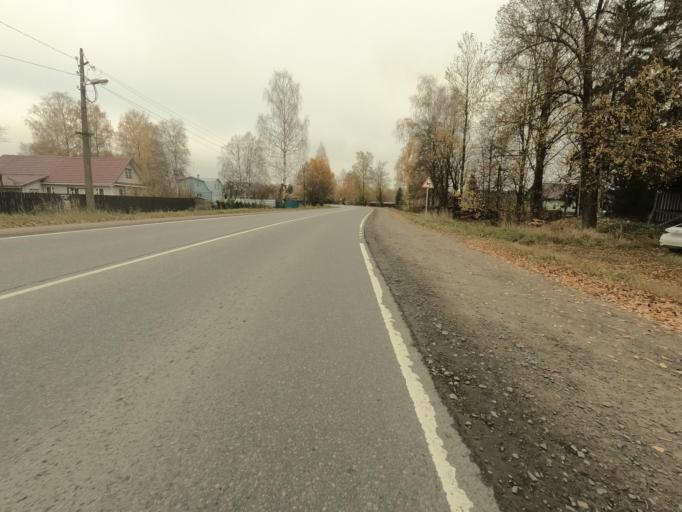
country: RU
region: Leningrad
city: Pavlovo
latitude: 59.8092
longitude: 30.8891
